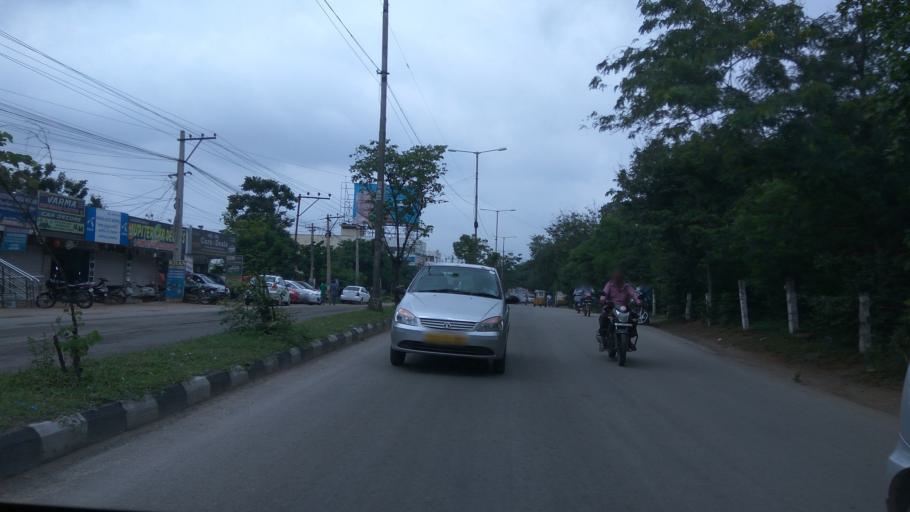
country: IN
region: Telangana
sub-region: Rangareddi
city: Secunderabad
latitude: 17.4833
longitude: 78.5436
